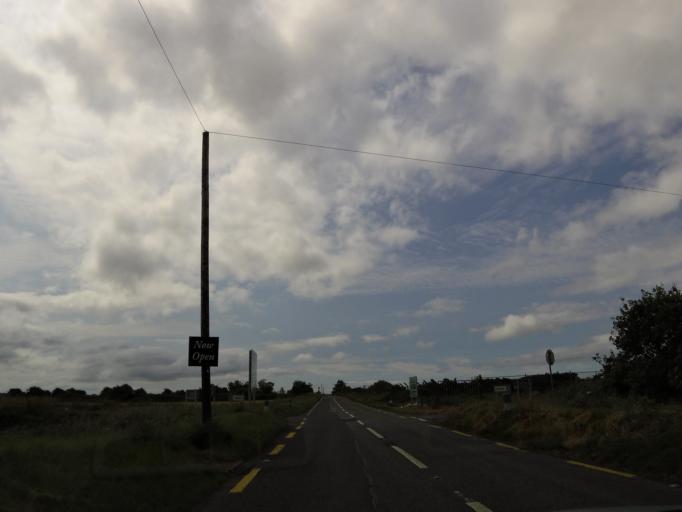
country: IE
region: Munster
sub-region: An Clar
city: Kilrush
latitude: 52.6734
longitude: -9.5567
